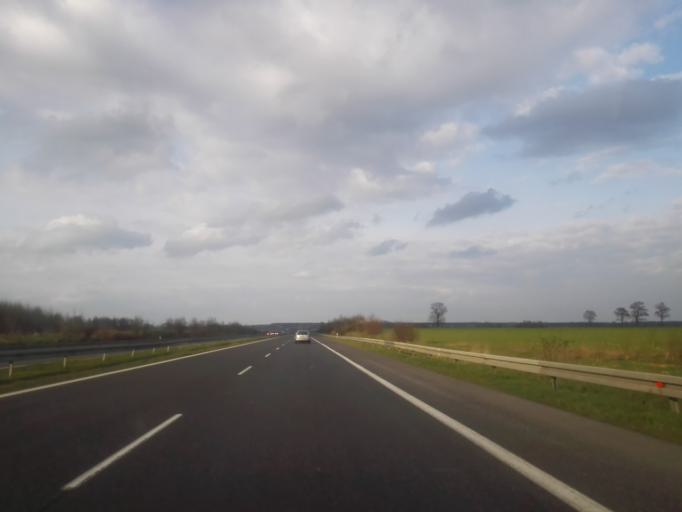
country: PL
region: Lodz Voivodeship
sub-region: Powiat piotrkowski
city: Wola Krzysztoporska
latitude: 51.3051
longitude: 19.5596
